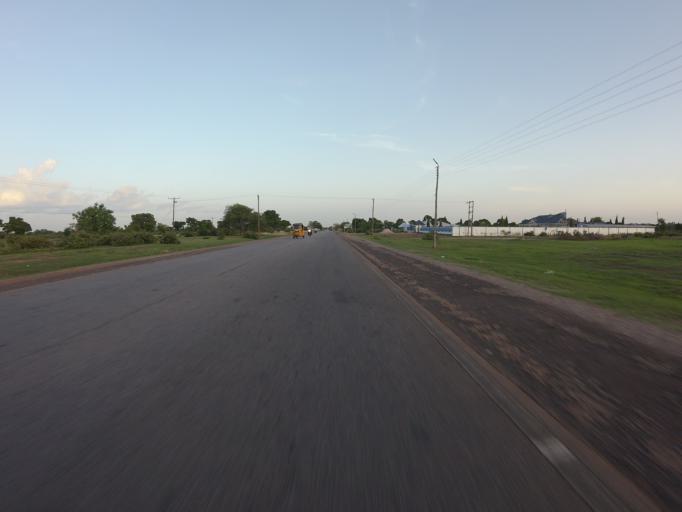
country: GH
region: Upper East
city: Navrongo
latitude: 10.9430
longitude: -1.0926
